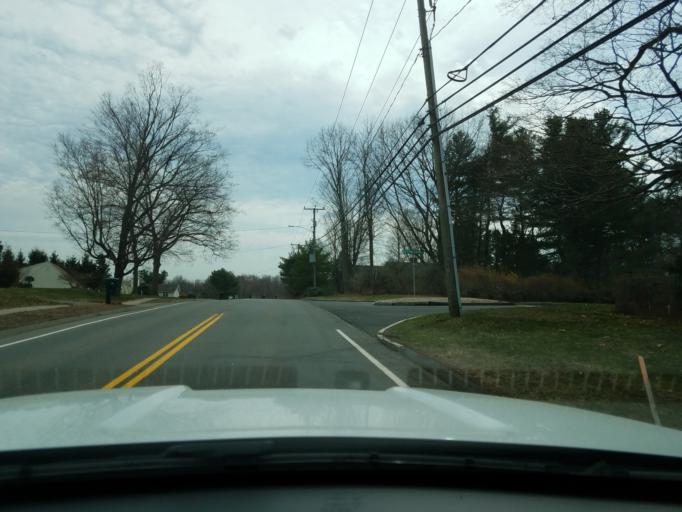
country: US
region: Connecticut
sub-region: Hartford County
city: Newington
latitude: 41.6611
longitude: -72.6862
